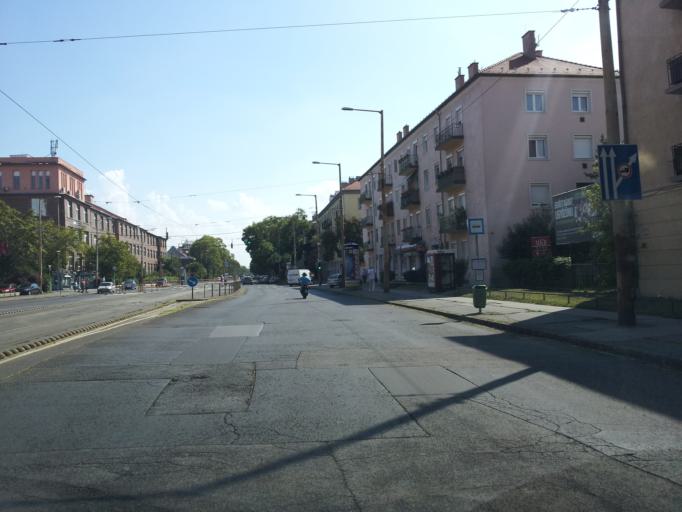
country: HU
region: Budapest
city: Budapest XI. keruelet
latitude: 47.4679
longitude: 19.0442
